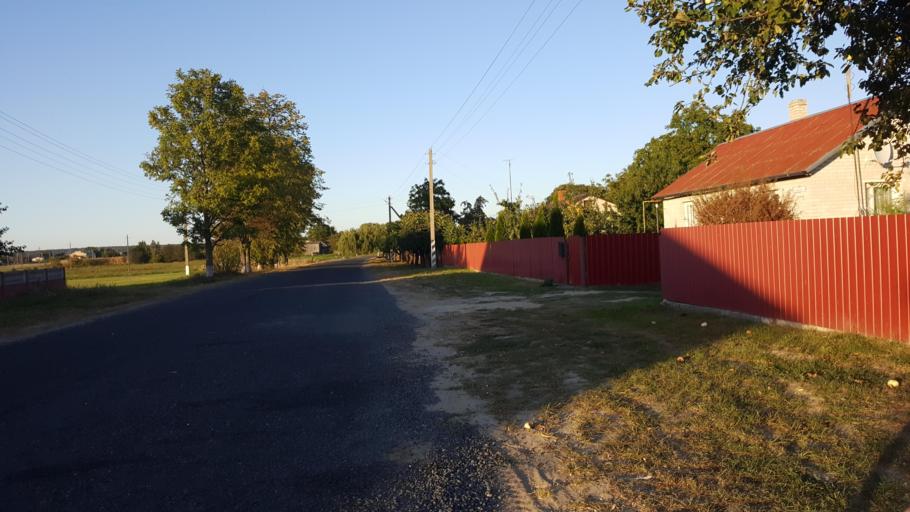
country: BY
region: Brest
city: Vysokaye
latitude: 52.2965
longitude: 23.4830
